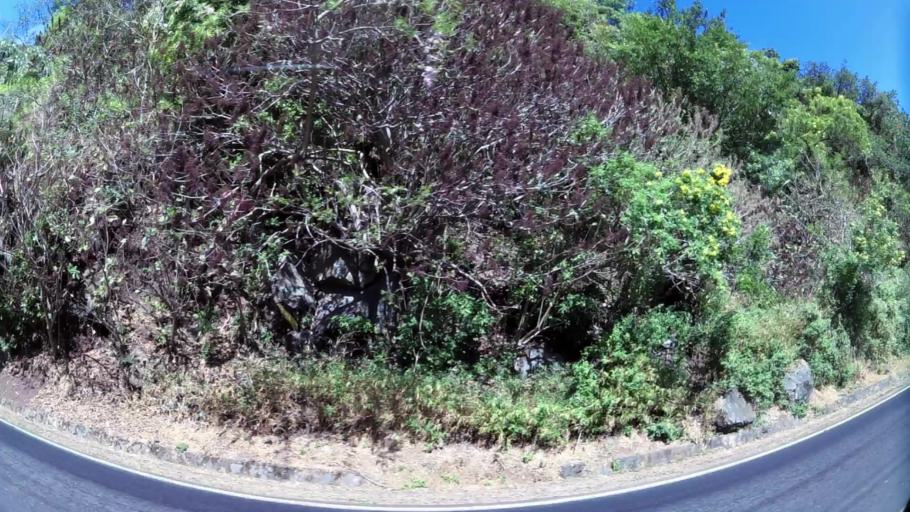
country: SV
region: Sonsonate
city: Juayua
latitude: 13.8496
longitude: -89.7668
